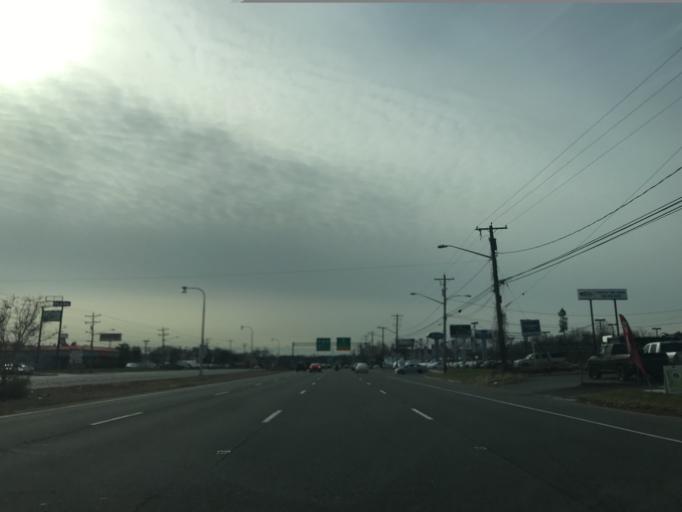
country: US
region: Delaware
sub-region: New Castle County
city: Wilmington Manor
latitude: 39.6579
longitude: -75.6130
